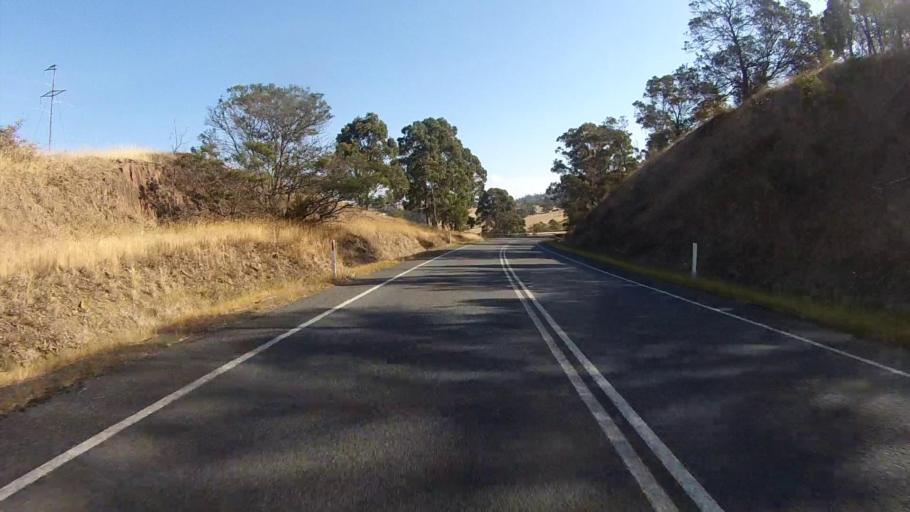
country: AU
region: Tasmania
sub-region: Sorell
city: Sorell
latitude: -42.7014
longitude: 147.5235
